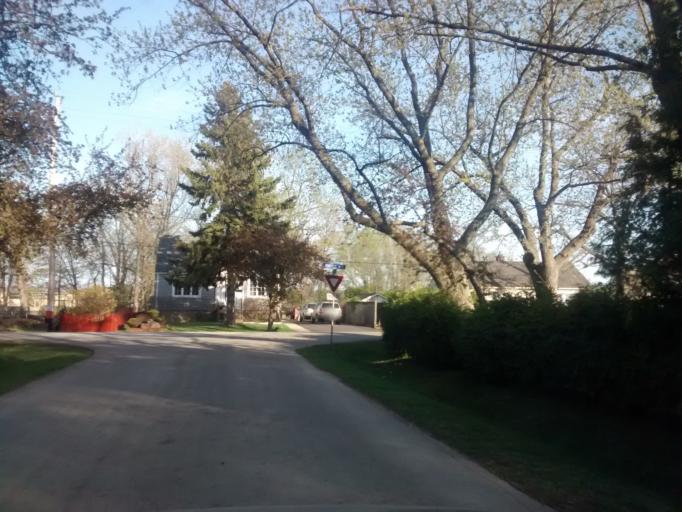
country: CA
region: Ontario
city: Burlington
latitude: 43.3434
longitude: -79.8080
